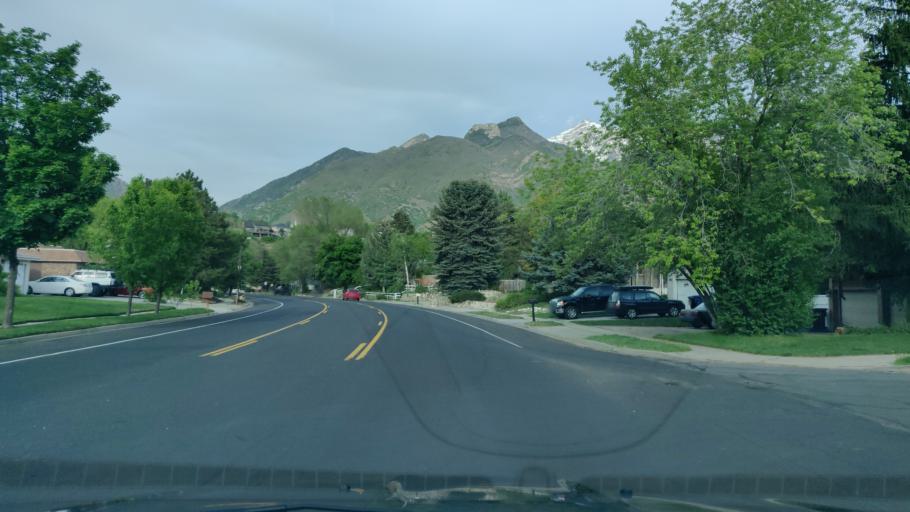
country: US
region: Utah
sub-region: Salt Lake County
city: Little Cottonwood Creek Valley
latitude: 40.6022
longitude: -111.8186
